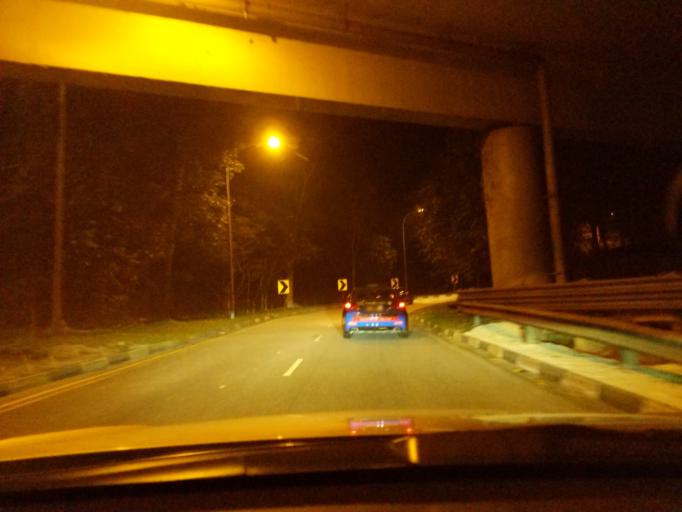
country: MY
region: Johor
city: Johor Bahru
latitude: 1.3649
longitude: 103.7763
